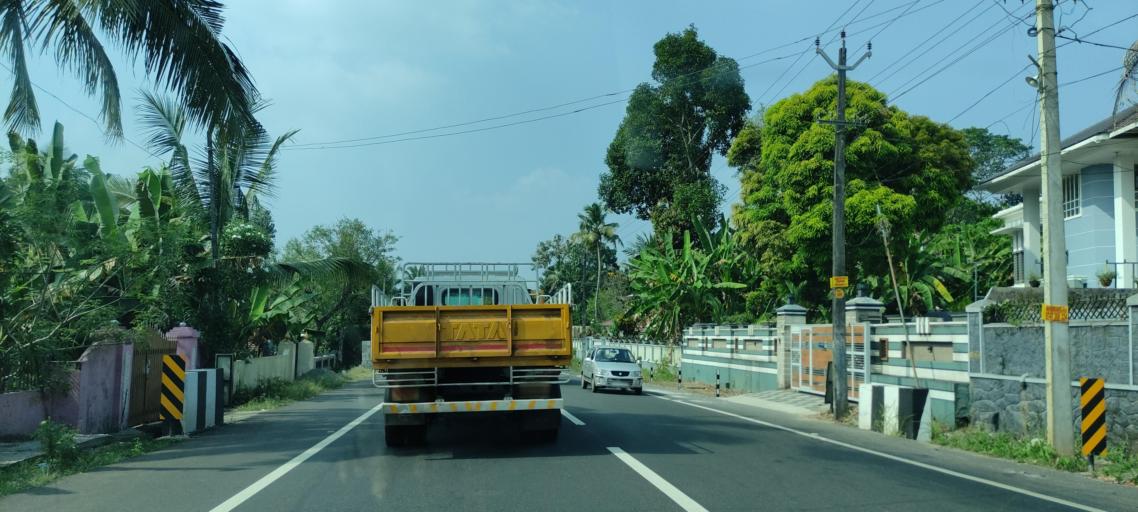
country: IN
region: Kerala
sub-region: Alappuzha
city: Chengannur
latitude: 9.2532
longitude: 76.6631
